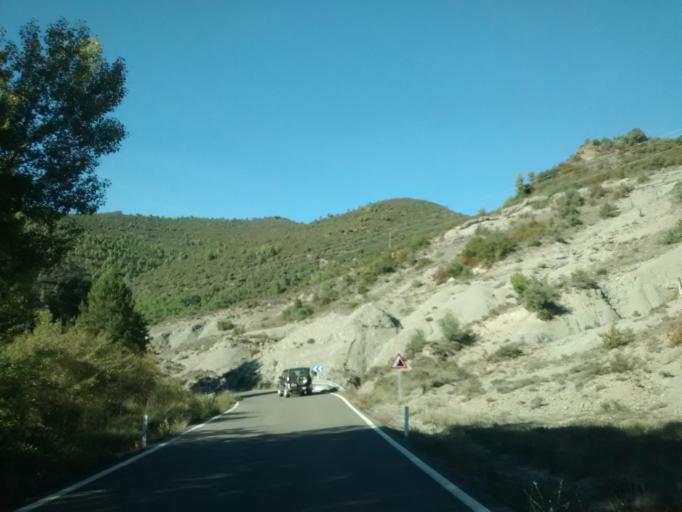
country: ES
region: Aragon
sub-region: Provincia de Huesca
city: Loarre
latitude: 42.3842
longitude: -0.6990
